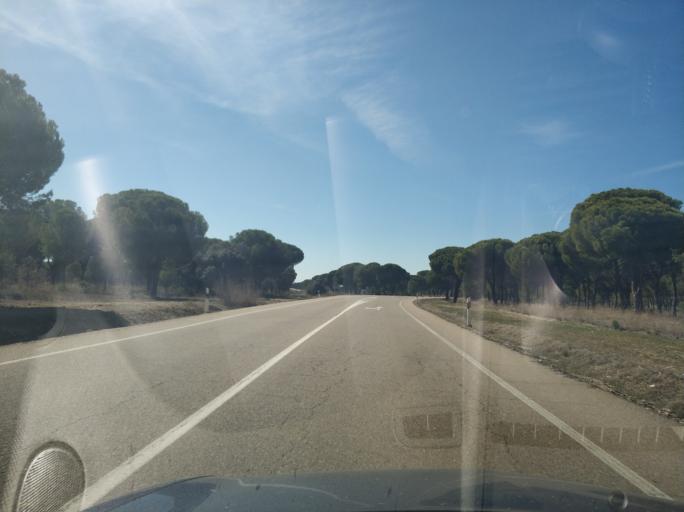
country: ES
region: Castille and Leon
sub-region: Provincia de Valladolid
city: Tudela de Duero
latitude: 41.5688
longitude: -4.5925
